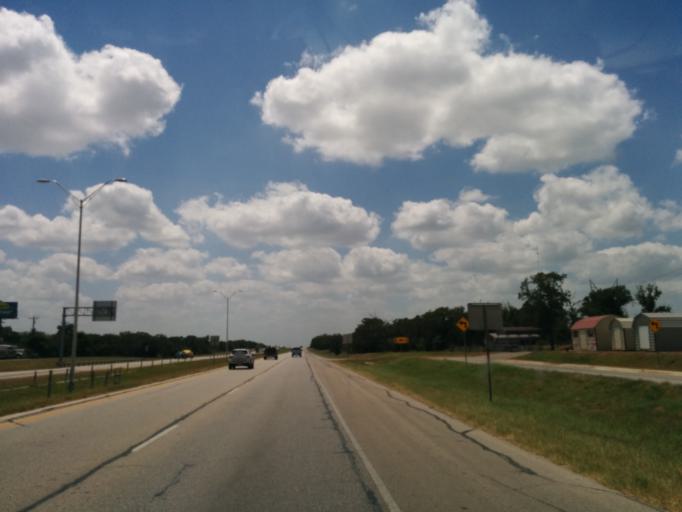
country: US
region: Texas
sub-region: Bastrop County
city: Bastrop
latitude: 30.1110
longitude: -97.3819
